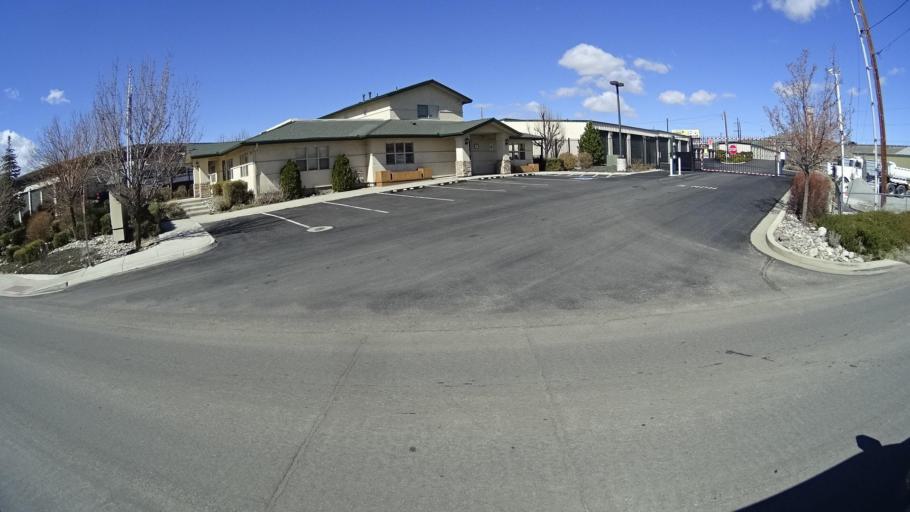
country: US
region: Nevada
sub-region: Washoe County
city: Golden Valley
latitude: 39.5860
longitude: -119.8249
